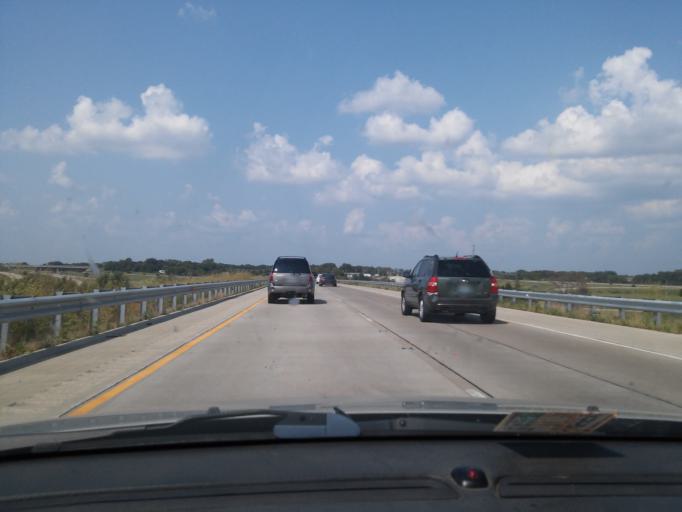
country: US
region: Illinois
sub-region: McLean County
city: Bloomington
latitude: 40.4406
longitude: -89.0228
